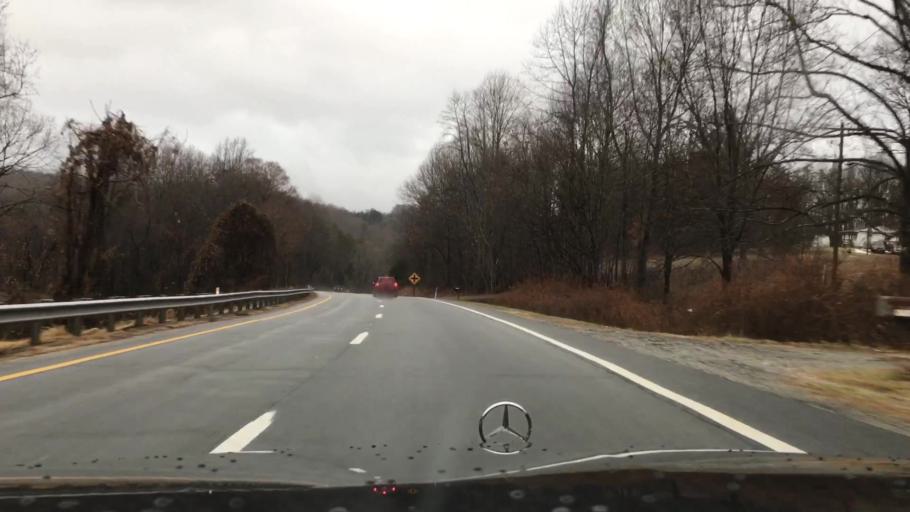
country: US
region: Virginia
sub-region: Nelson County
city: Nellysford
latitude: 37.8442
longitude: -78.7904
